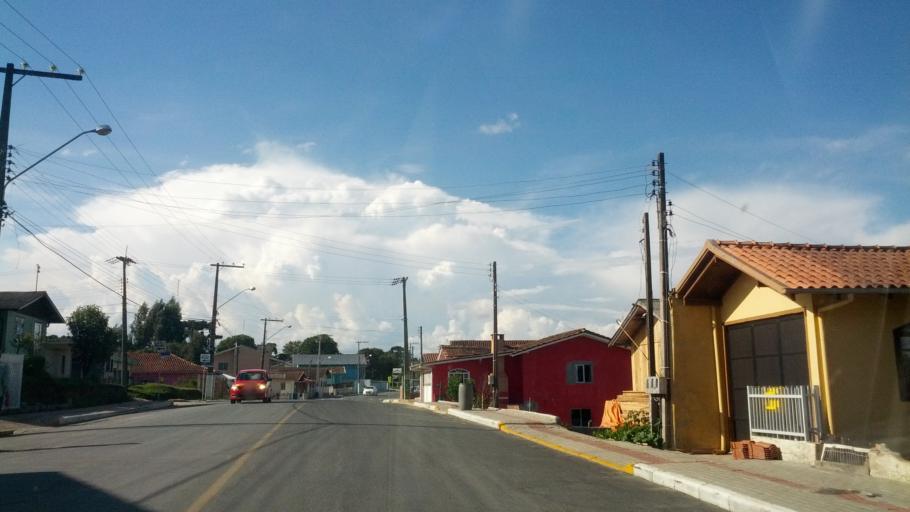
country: BR
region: Santa Catarina
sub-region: Otacilio Costa
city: Otacilio Costa
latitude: -27.4931
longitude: -50.1231
